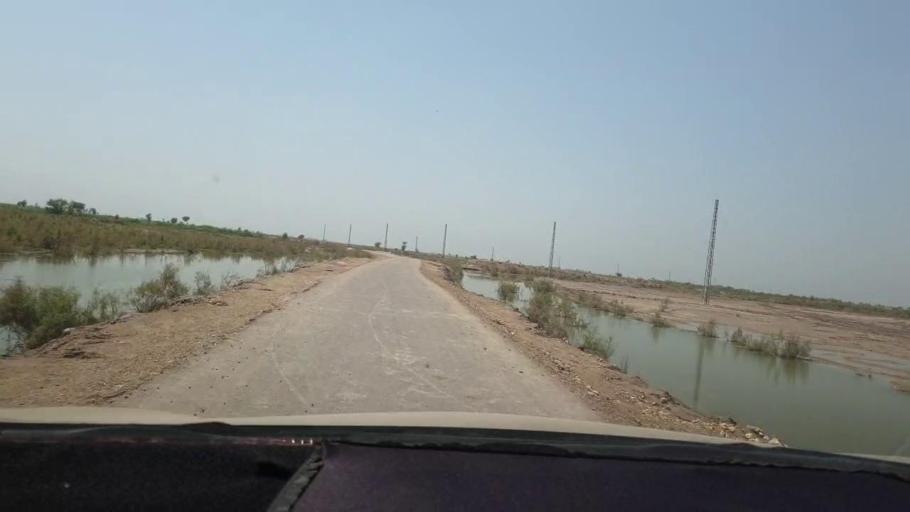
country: PK
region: Sindh
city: Shahdadkot
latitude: 27.8339
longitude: 67.8834
